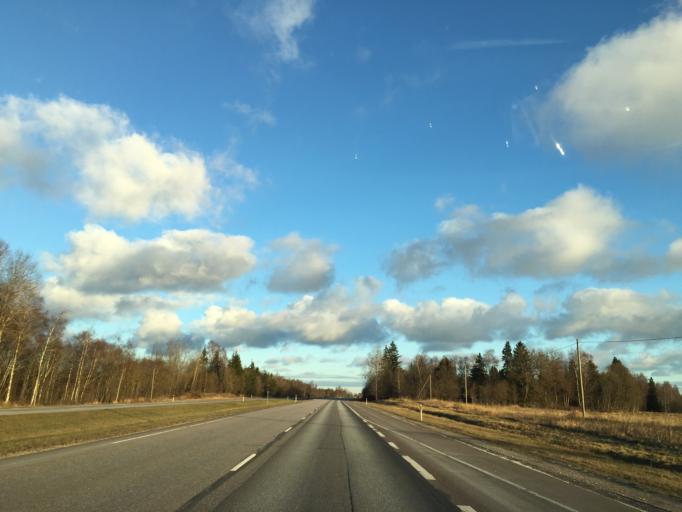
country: EE
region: Harju
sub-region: Saue linn
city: Saue
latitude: 59.2857
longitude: 24.5356
